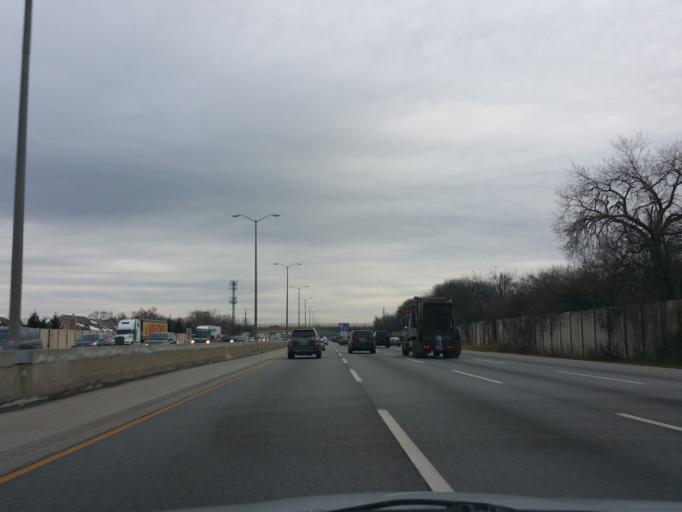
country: US
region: Illinois
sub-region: Cook County
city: Western Springs
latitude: 41.7934
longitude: -87.9082
